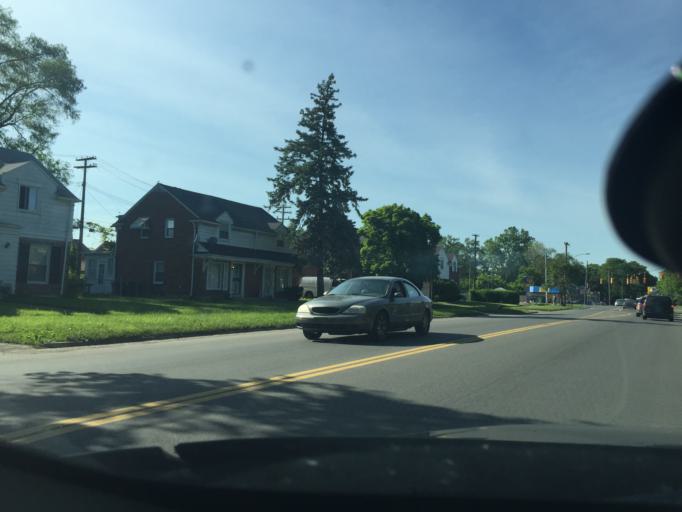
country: US
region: Michigan
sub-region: Oakland County
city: Southfield
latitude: 42.4139
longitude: -83.2380
